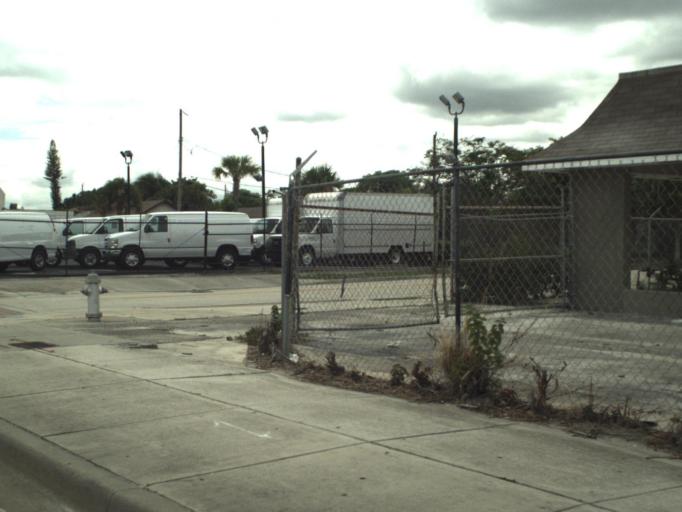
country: US
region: Florida
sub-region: Palm Beach County
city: Riviera Beach
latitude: 26.7612
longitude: -80.0554
